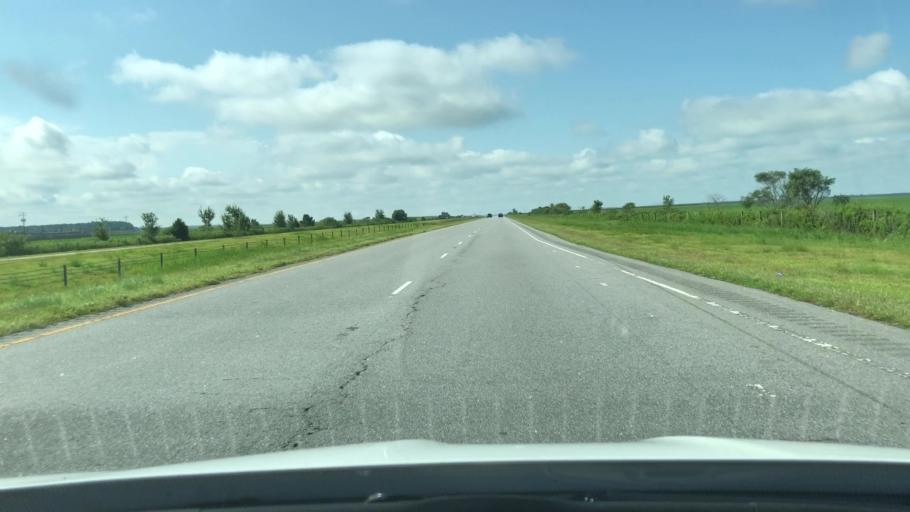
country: US
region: North Carolina
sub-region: Pasquotank County
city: Elizabeth City
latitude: 36.3600
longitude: -76.3156
